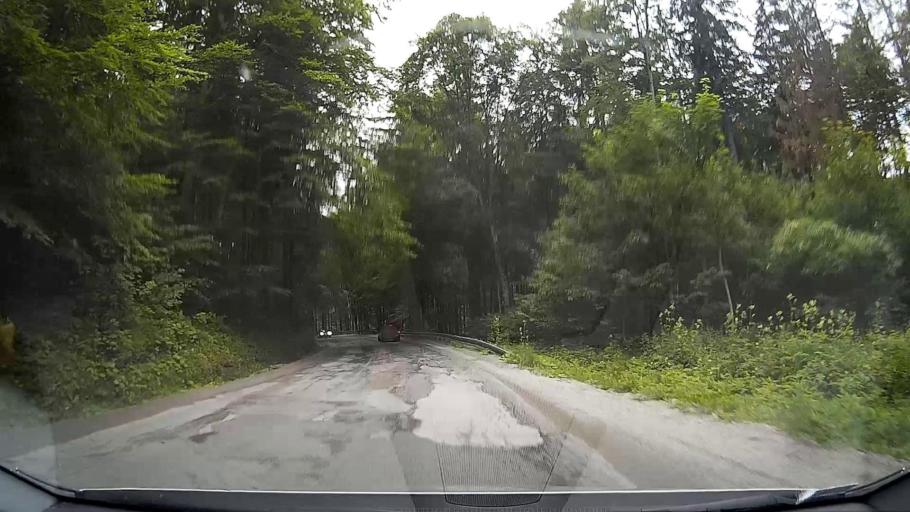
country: SK
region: Banskobystricky
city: Revuca
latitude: 48.7920
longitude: 20.1314
